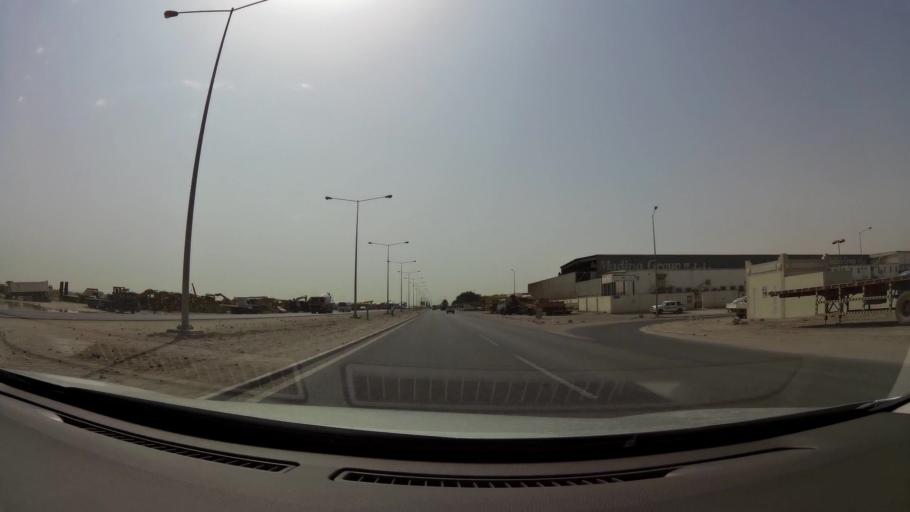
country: QA
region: Al Wakrah
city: Al Wukayr
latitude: 25.1815
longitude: 51.4629
